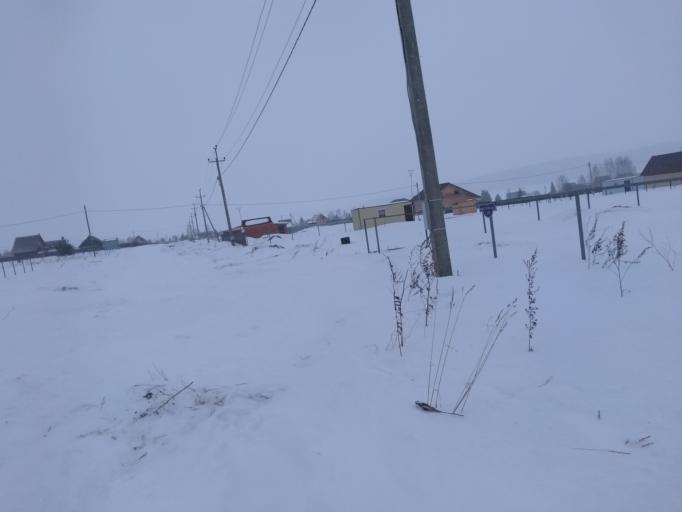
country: RU
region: Perm
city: Sylva
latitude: 57.8465
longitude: 56.7844
